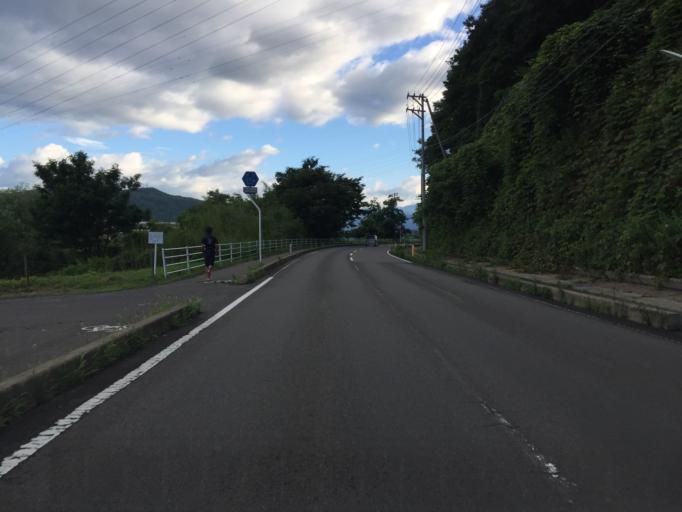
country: JP
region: Fukushima
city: Fukushima-shi
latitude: 37.7542
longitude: 140.4874
